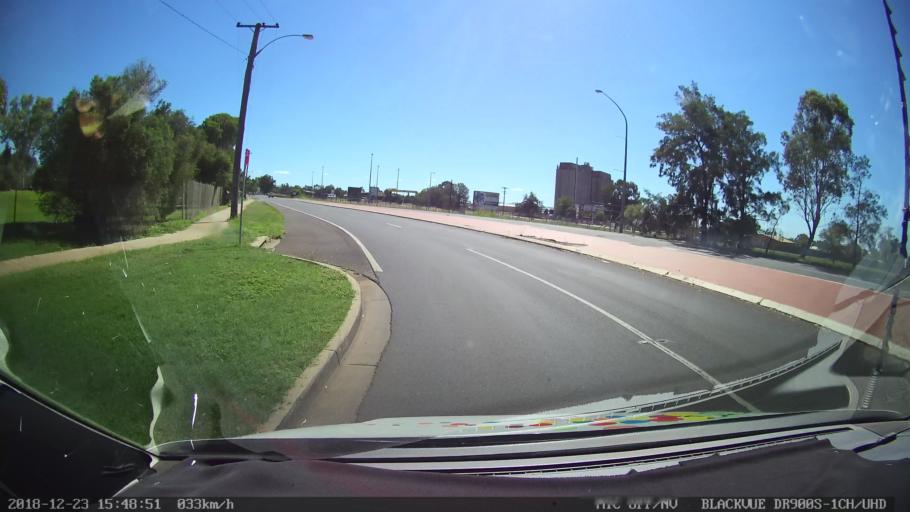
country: AU
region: New South Wales
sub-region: Tamworth Municipality
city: South Tamworth
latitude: -31.0959
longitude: 150.9105
